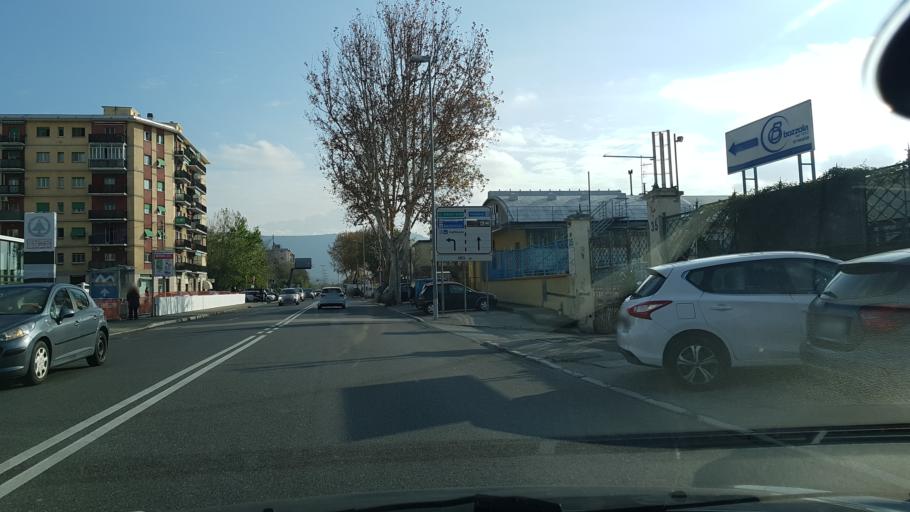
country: IT
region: Friuli Venezia Giulia
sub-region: Provincia di Trieste
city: Domio
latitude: 45.6207
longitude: 13.8088
